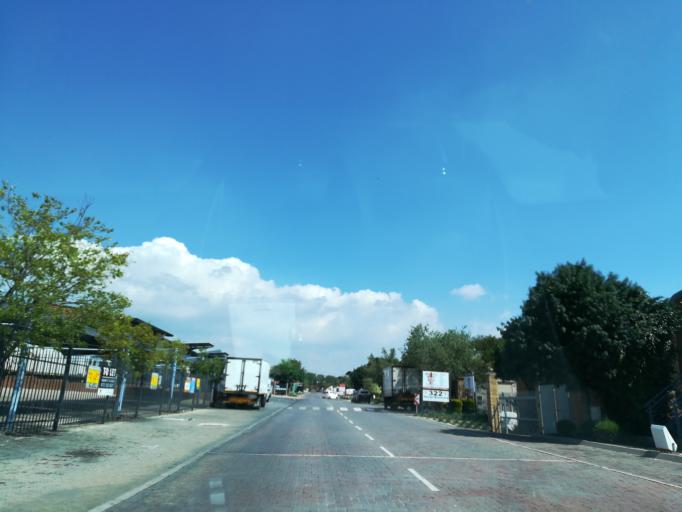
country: ZA
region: Gauteng
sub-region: City of Johannesburg Metropolitan Municipality
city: Diepsloot
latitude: -26.0351
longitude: 27.9594
